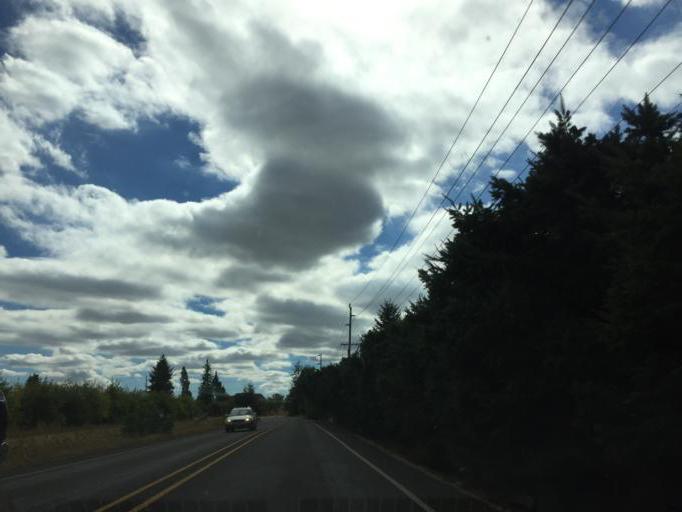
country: US
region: Oregon
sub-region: Marion County
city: Woodburn
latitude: 45.1236
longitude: -122.8050
